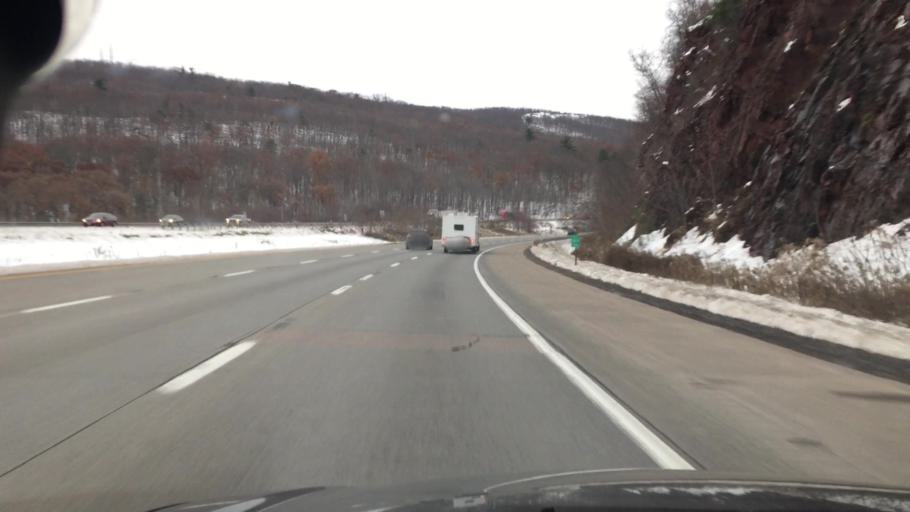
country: US
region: Pennsylvania
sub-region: Luzerne County
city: Ashley
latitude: 41.1880
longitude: -75.9186
